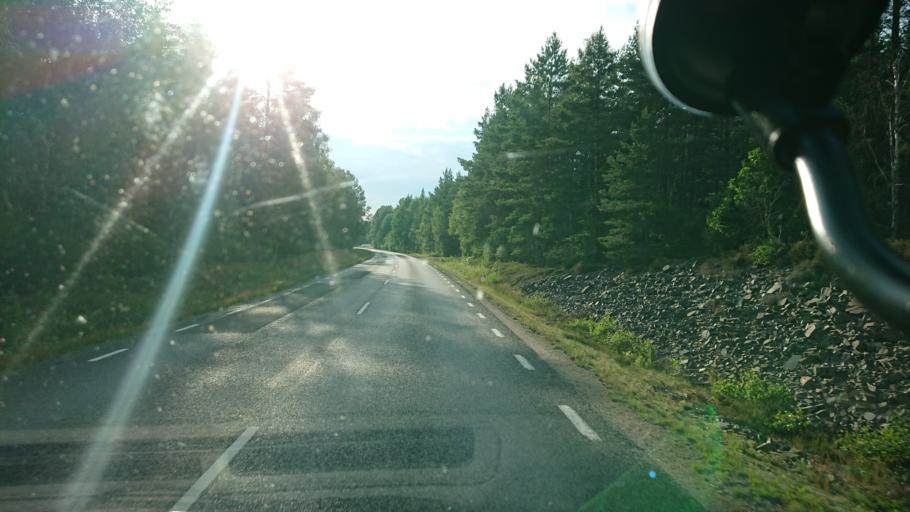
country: SE
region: Kronoberg
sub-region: Vaxjo Kommun
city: Rottne
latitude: 57.0315
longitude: 14.9691
